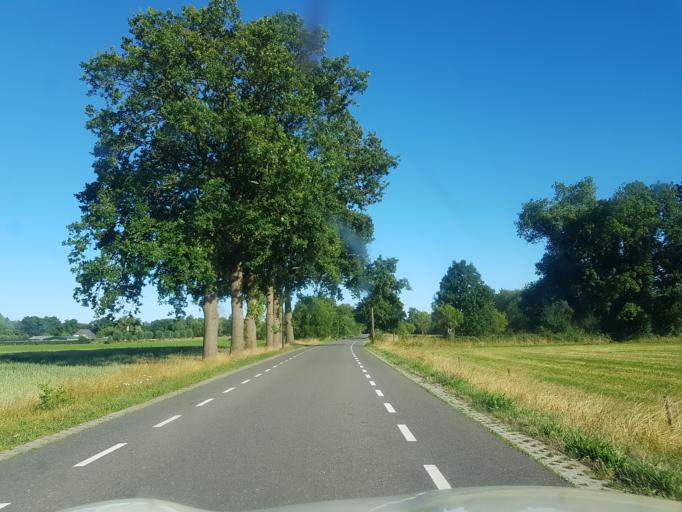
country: NL
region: Gelderland
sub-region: Gemeente Apeldoorn
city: Beekbergen
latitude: 52.1784
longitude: 6.0157
